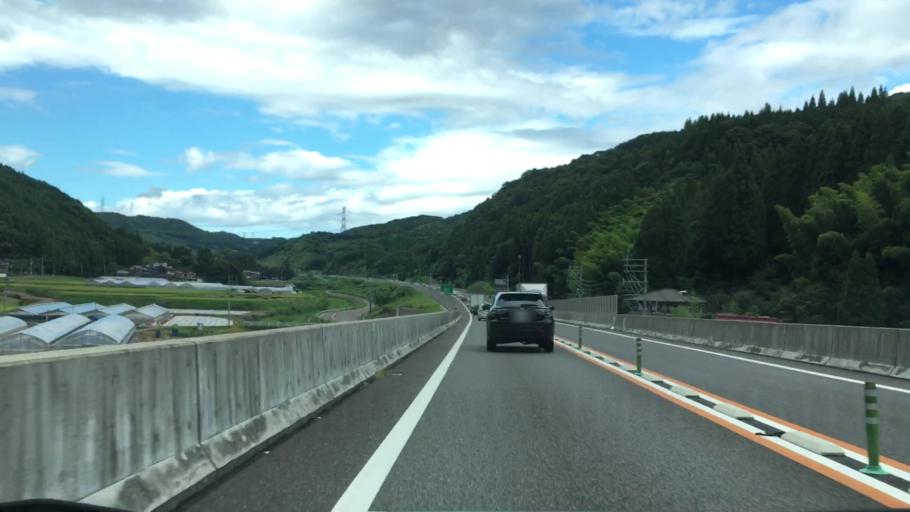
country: JP
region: Saga Prefecture
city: Karatsu
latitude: 33.3758
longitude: 129.9318
